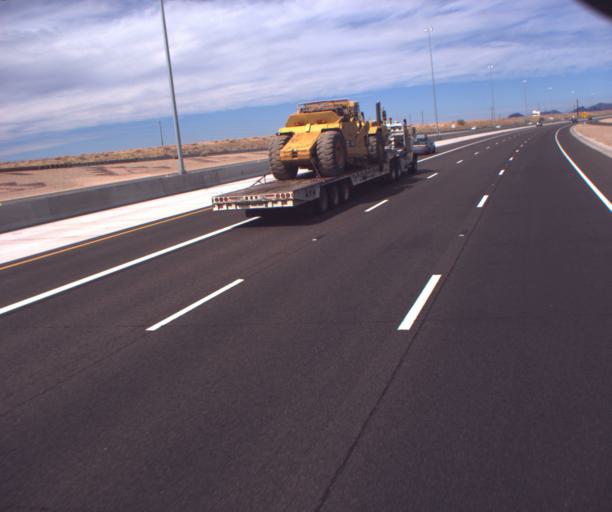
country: US
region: Arizona
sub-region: Pinal County
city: Apache Junction
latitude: 33.4531
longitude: -111.6713
